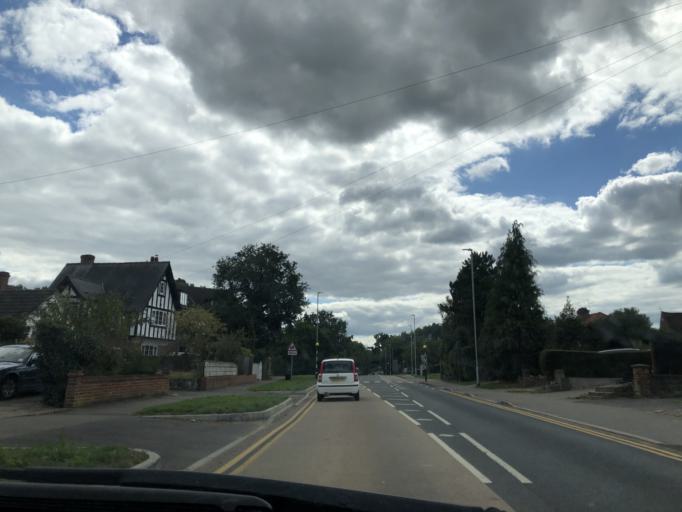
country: GB
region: England
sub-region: Kent
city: Edenbridge
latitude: 51.2043
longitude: 0.0623
